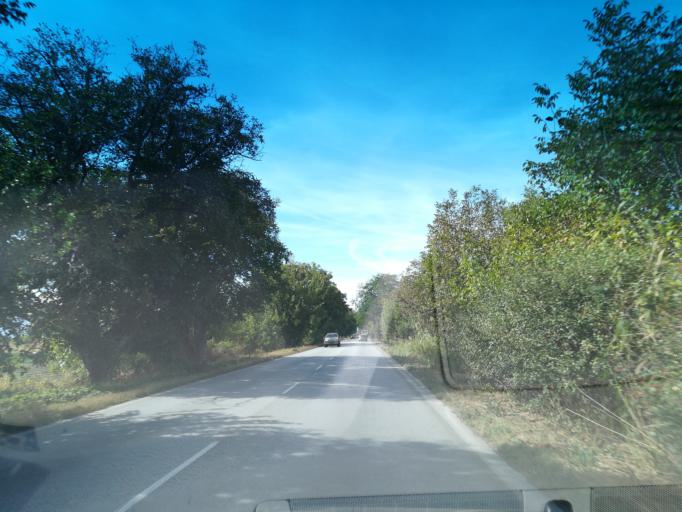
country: BG
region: Plovdiv
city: Stamboliyski
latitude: 42.1347
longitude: 24.6234
